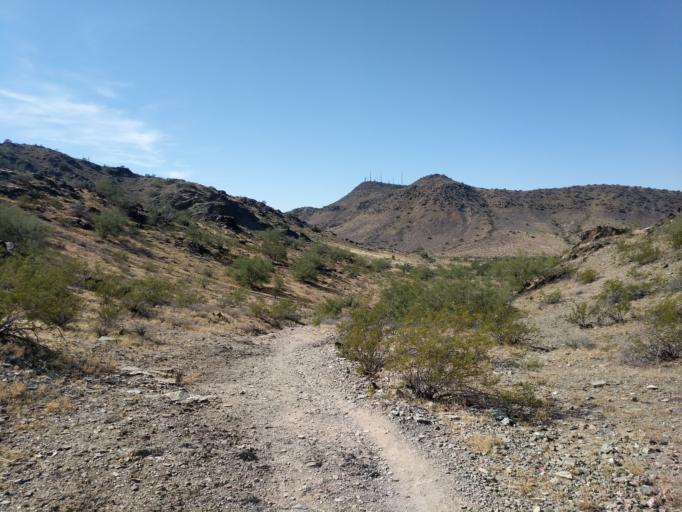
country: US
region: Arizona
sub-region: Maricopa County
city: Glendale
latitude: 33.5914
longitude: -112.0673
